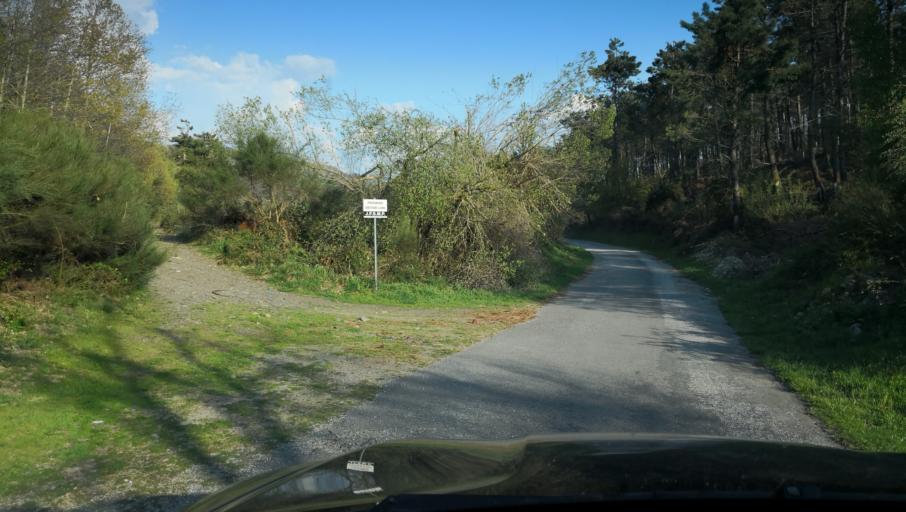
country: PT
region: Vila Real
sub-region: Vila Real
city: Vila Real
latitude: 41.3087
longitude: -7.8467
